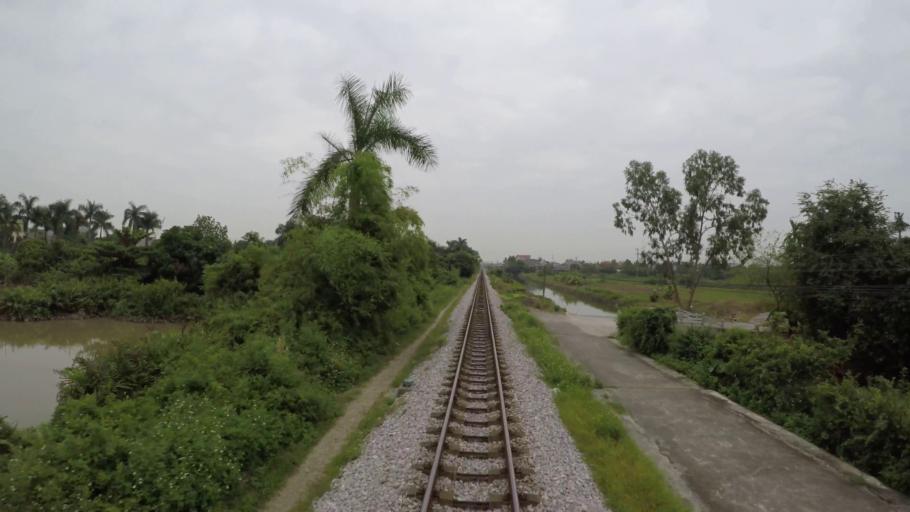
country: VN
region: Hai Phong
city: An Duong
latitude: 20.8917
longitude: 106.5924
